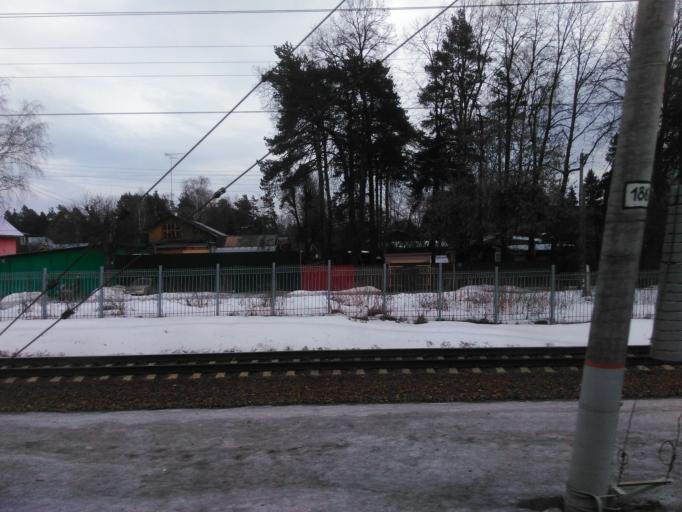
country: RU
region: Moskovskaya
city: Mamontovka
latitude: 55.9742
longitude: 37.8163
